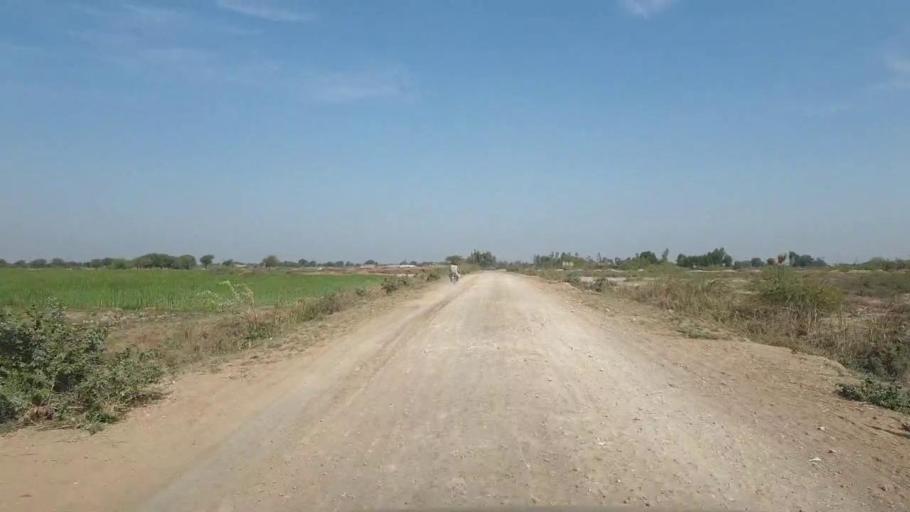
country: PK
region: Sindh
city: Samaro
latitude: 25.3798
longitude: 69.2590
